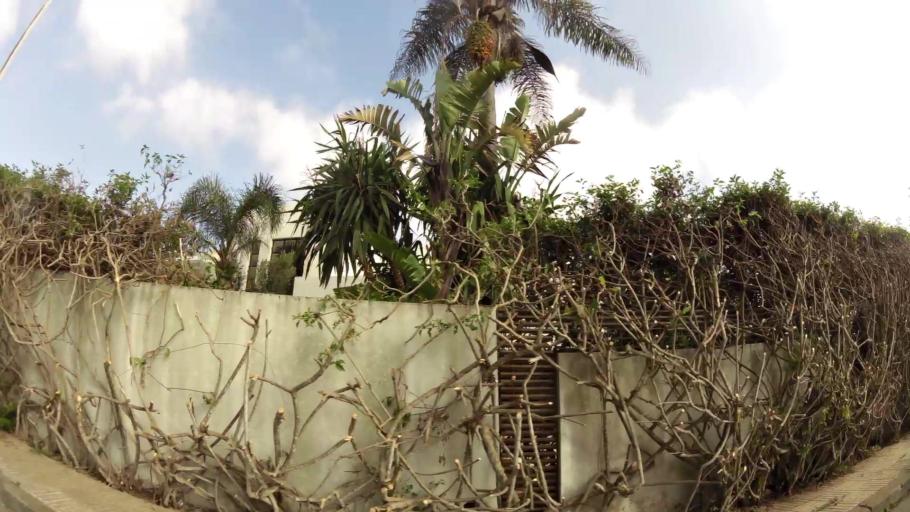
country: MA
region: Rabat-Sale-Zemmour-Zaer
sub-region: Rabat
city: Rabat
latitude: 33.9695
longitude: -6.8449
